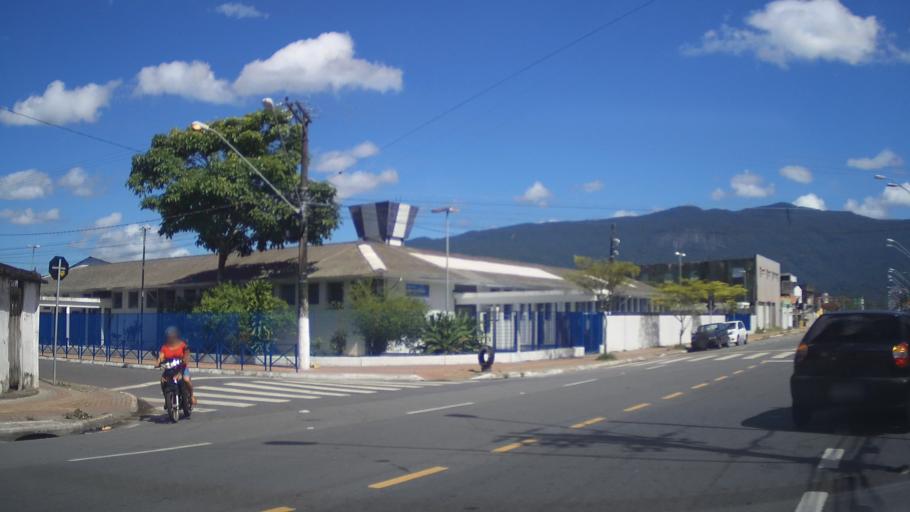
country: BR
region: Sao Paulo
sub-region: Mongagua
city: Mongagua
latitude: -24.0346
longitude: -46.5297
